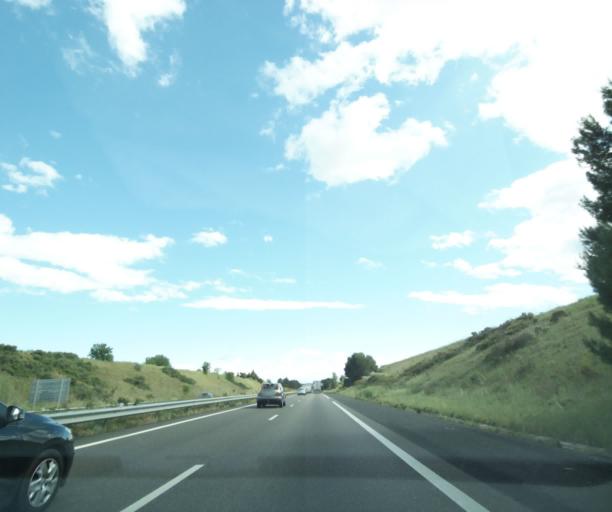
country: FR
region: Languedoc-Roussillon
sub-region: Departement du Gard
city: Garons
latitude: 43.7657
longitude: 4.4220
